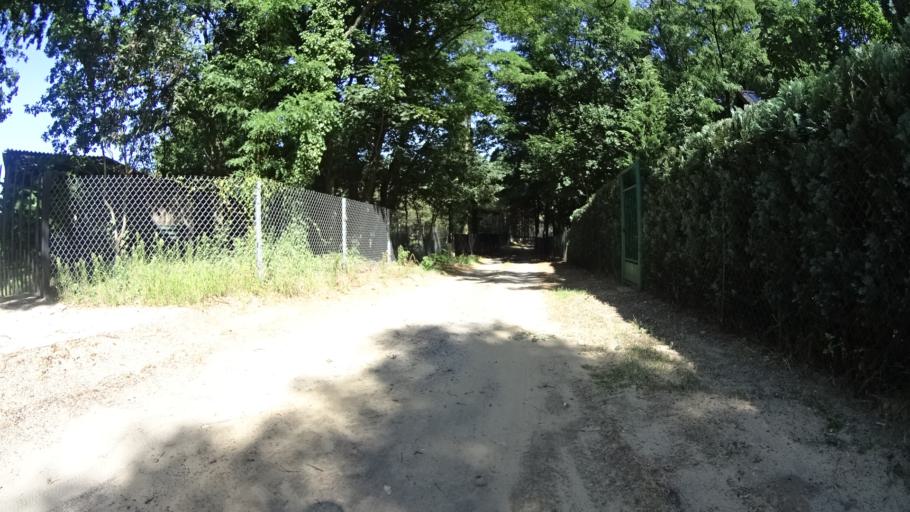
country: PL
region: Masovian Voivodeship
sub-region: Powiat bialobrzeski
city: Bialobrzegi
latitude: 51.6696
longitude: 20.9270
